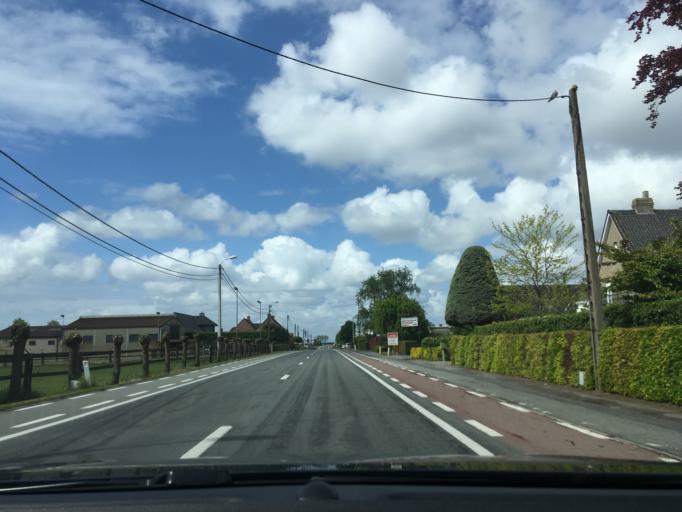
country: BE
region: Flanders
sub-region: Provincie West-Vlaanderen
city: Pittem
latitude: 50.9907
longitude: 3.2519
